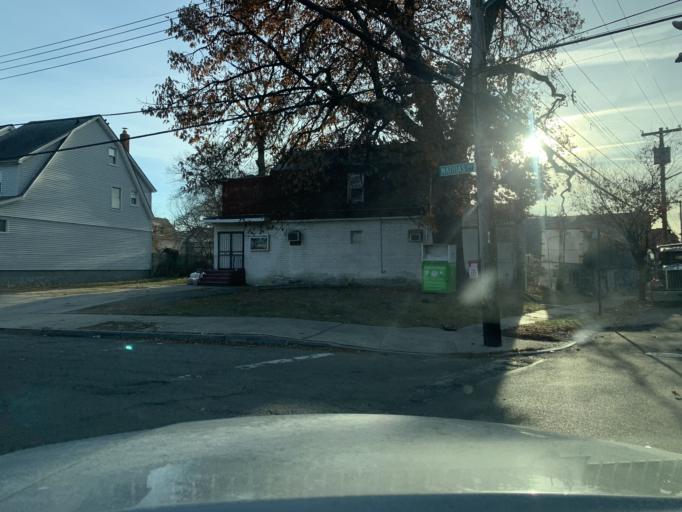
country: US
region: New York
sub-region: Queens County
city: Jamaica
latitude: 40.6908
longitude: -73.7871
